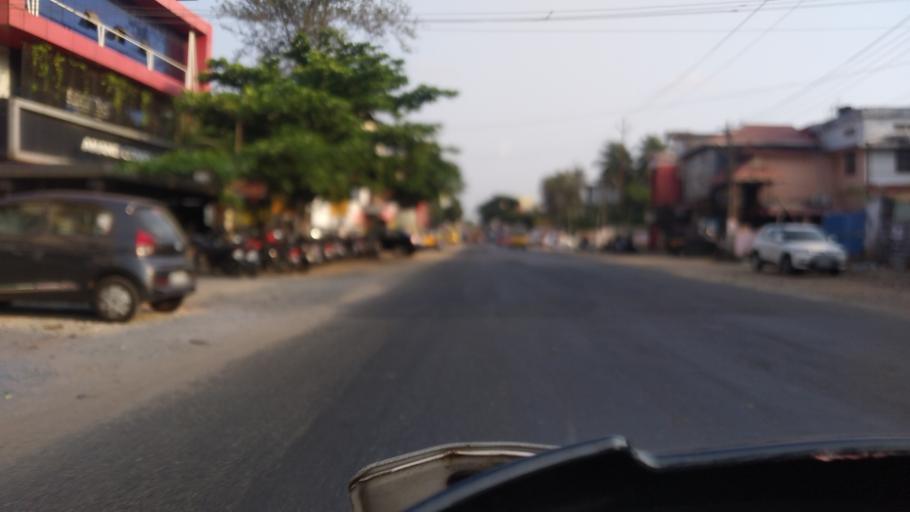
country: IN
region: Kerala
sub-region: Thrissur District
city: Thanniyam
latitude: 10.4166
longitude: 76.1064
